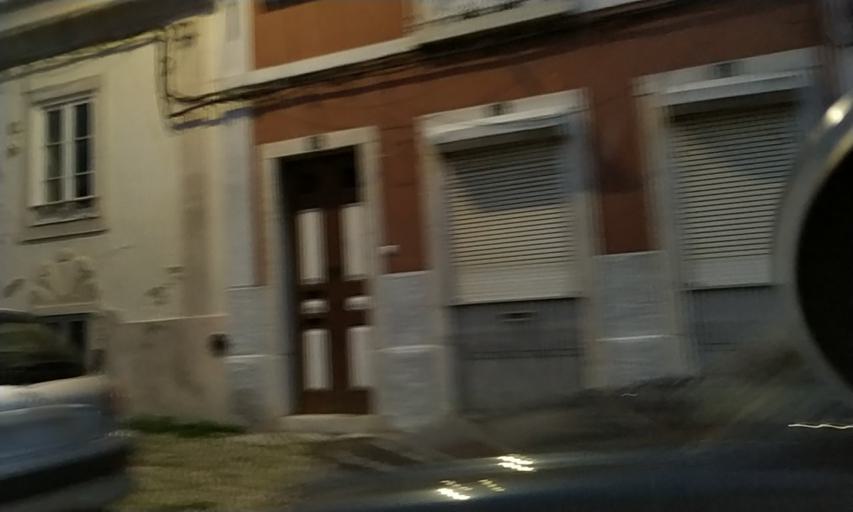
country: PT
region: Setubal
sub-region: Setubal
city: Setubal
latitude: 38.5266
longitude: -8.8880
